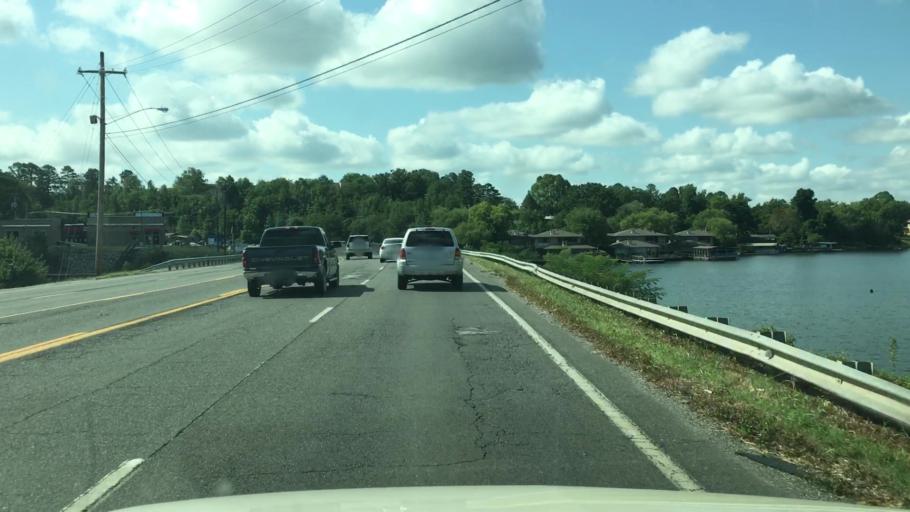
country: US
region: Arkansas
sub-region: Garland County
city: Piney
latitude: 34.4976
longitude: -93.1220
